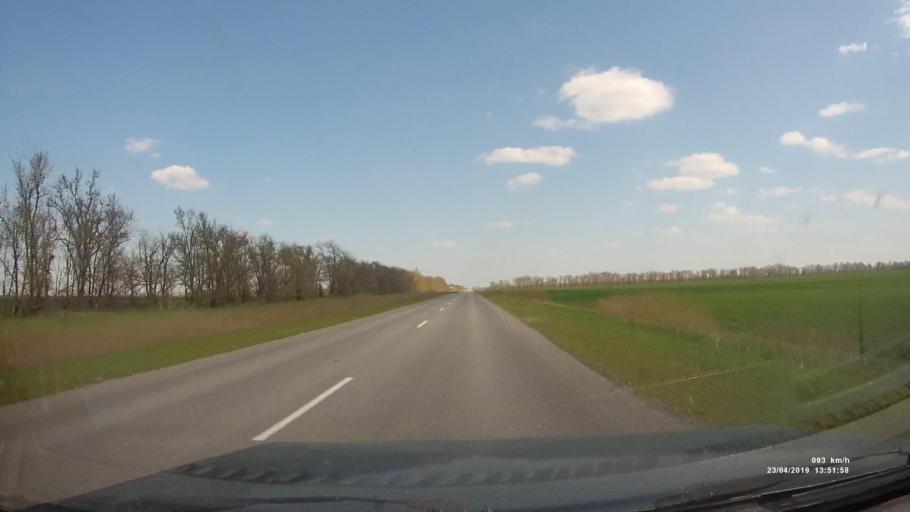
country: RU
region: Rostov
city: Remontnoye
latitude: 46.6004
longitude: 42.9444
